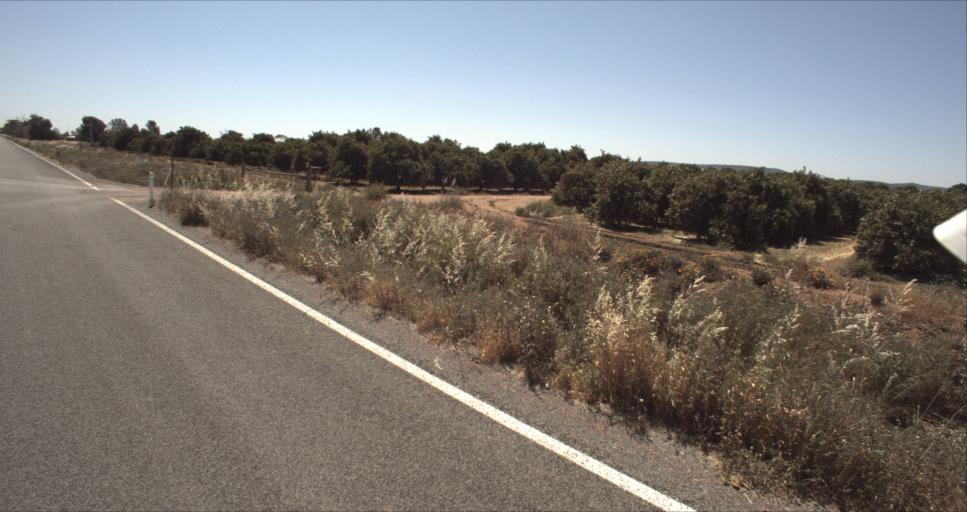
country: AU
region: New South Wales
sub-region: Leeton
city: Leeton
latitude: -34.5177
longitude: 146.4353
